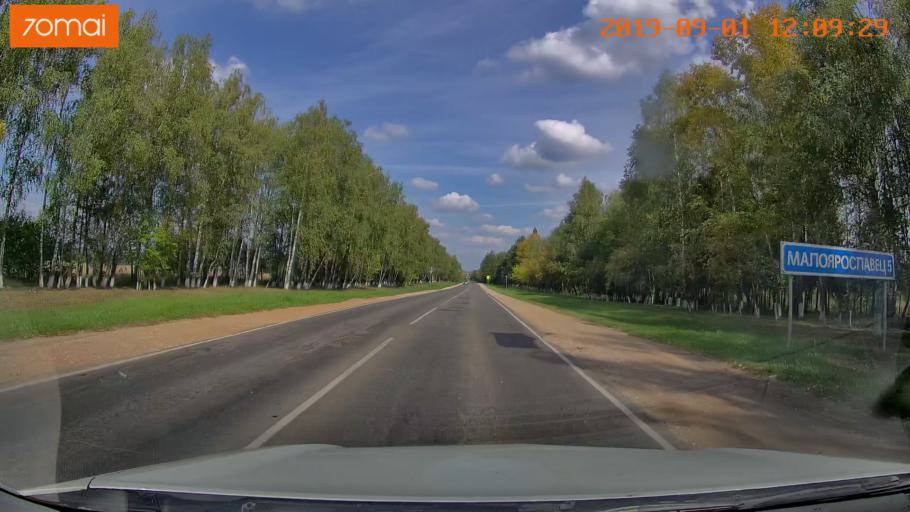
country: RU
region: Kaluga
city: Maloyaroslavets
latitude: 54.9811
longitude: 36.4264
